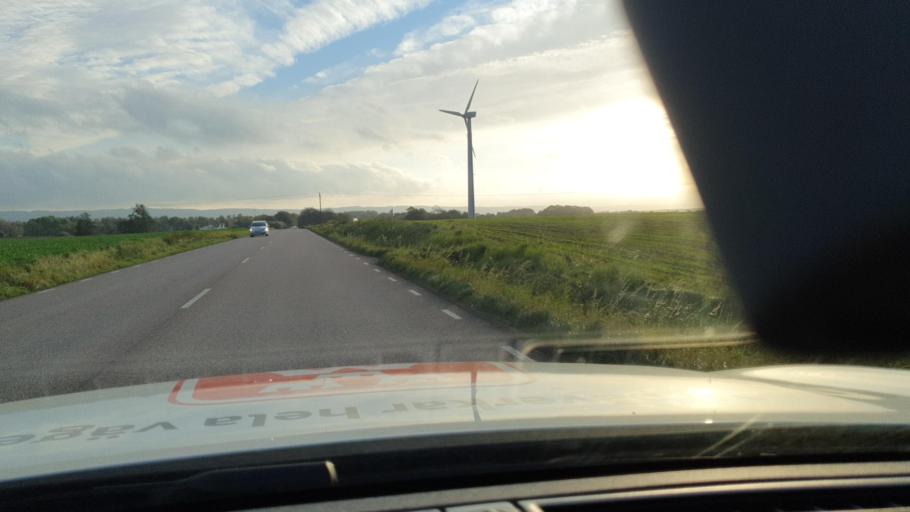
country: SE
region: Halland
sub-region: Laholms Kommun
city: Laholm
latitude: 56.4767
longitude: 13.0391
